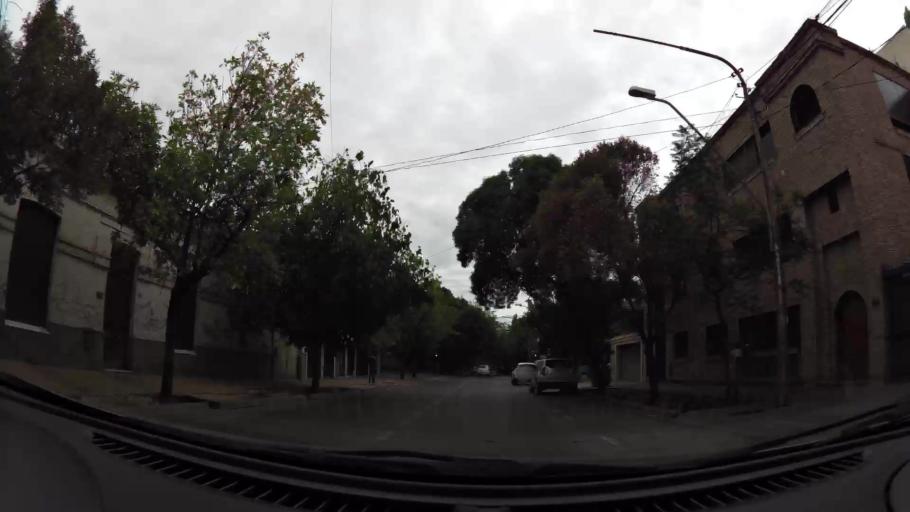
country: AR
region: Mendoza
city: Mendoza
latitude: -32.8851
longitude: -68.8588
